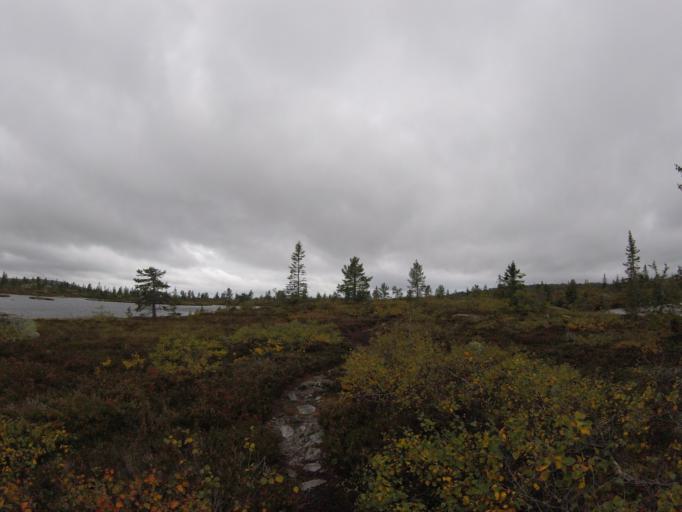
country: NO
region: Buskerud
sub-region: Flesberg
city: Lampeland
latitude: 59.7748
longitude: 9.3901
